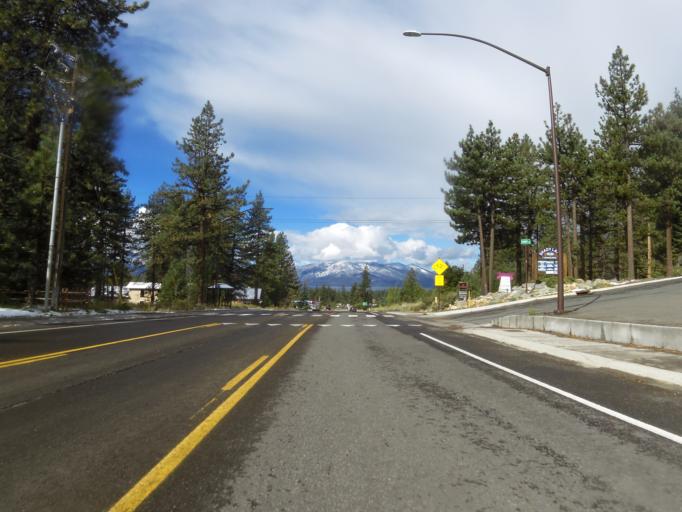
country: US
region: Nevada
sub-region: Douglas County
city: Kingsbury
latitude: 38.9683
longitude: -119.9311
